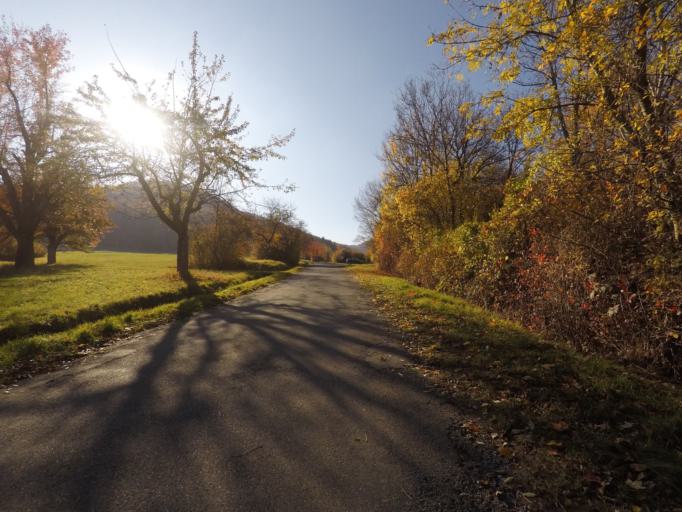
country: DE
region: Baden-Wuerttemberg
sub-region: Tuebingen Region
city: Pfullingen
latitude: 48.4450
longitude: 9.2412
